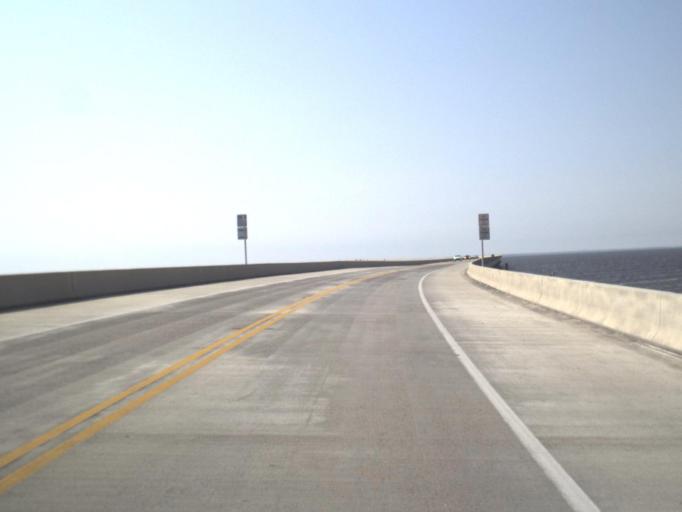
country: US
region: Florida
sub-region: Franklin County
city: Eastpoint
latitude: 29.7225
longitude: -84.8881
